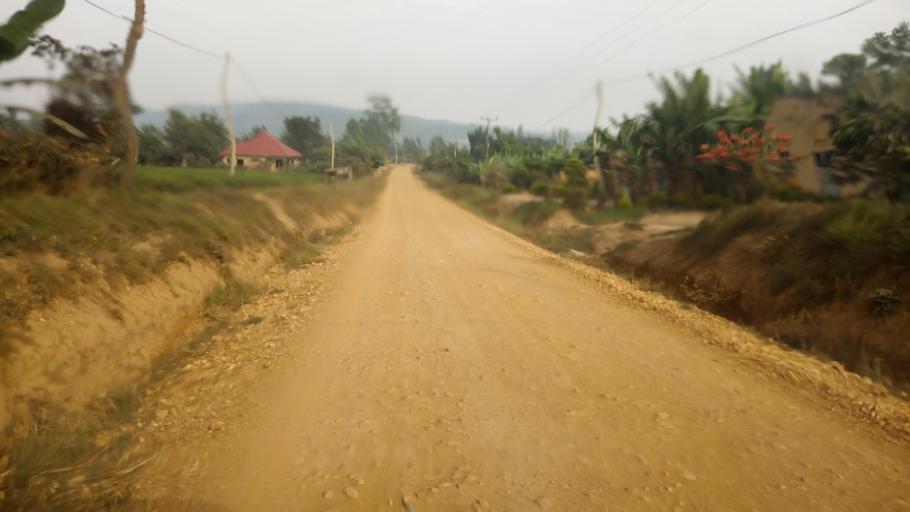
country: UG
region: Western Region
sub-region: Kanungu District
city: Ntungamo
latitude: -0.8396
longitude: 29.6513
